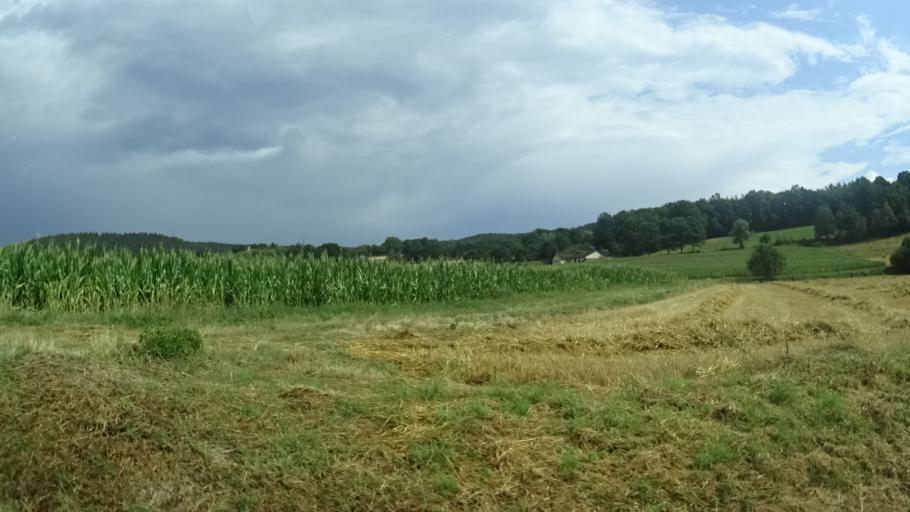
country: DE
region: Hesse
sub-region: Regierungsbezirk Kassel
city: Niederaula
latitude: 50.7906
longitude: 9.6134
